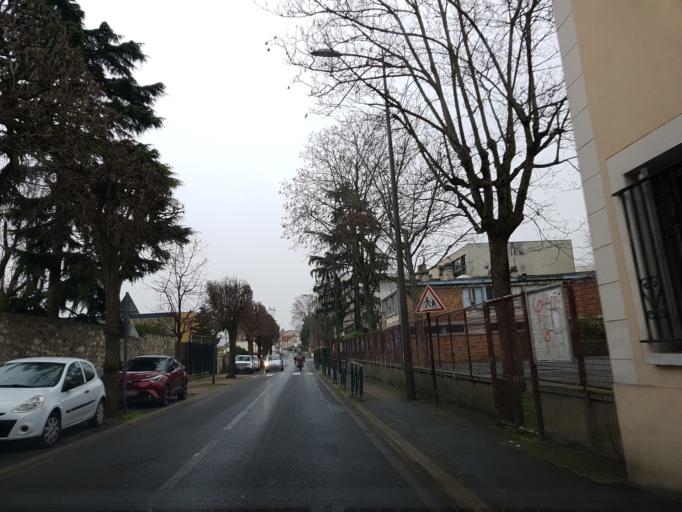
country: FR
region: Ile-de-France
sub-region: Departement du Val-de-Marne
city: Thiais
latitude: 48.7636
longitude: 2.3936
